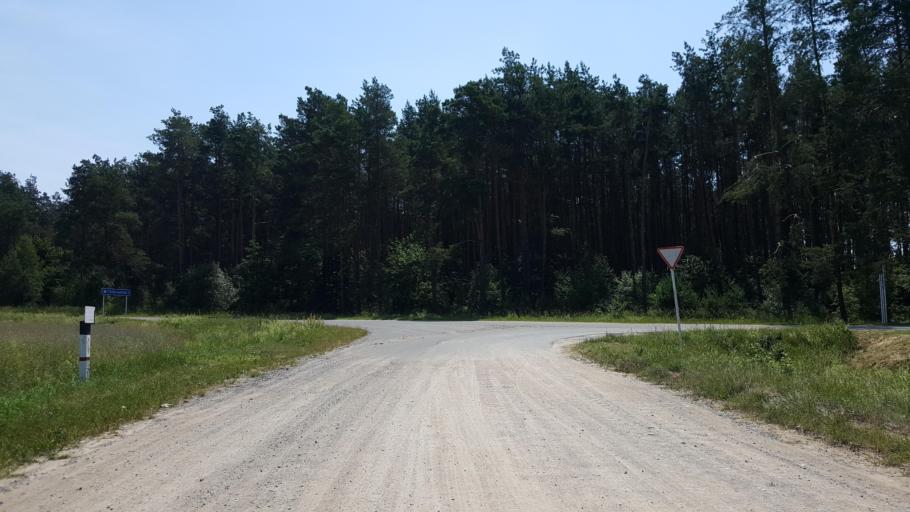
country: BY
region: Brest
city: Kamyanyets
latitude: 52.4088
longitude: 23.8389
